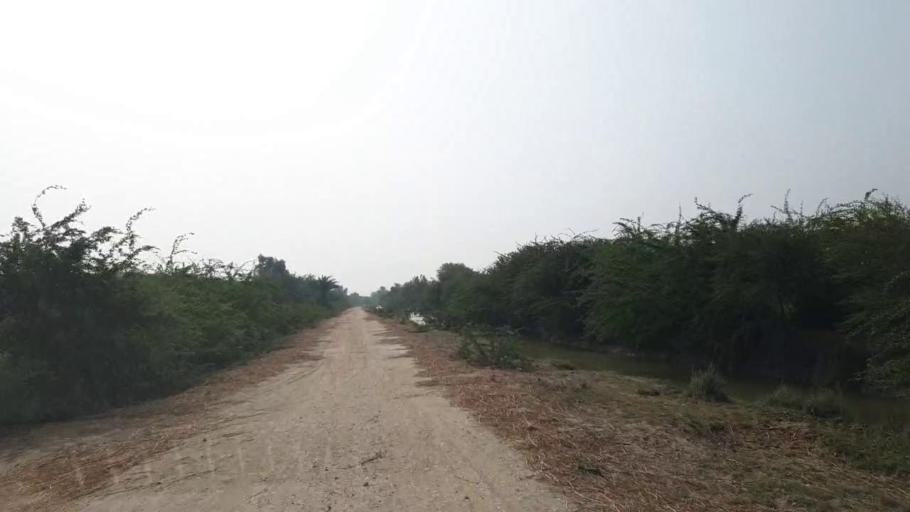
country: PK
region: Sindh
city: Kario
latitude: 24.7589
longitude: 68.5637
